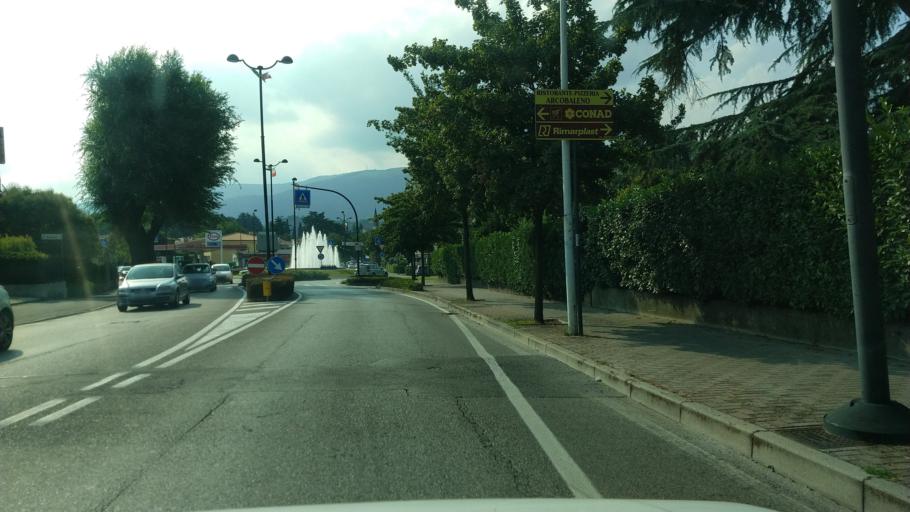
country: IT
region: Veneto
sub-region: Provincia di Vicenza
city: Bassano del Grappa
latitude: 45.7654
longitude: 11.7282
